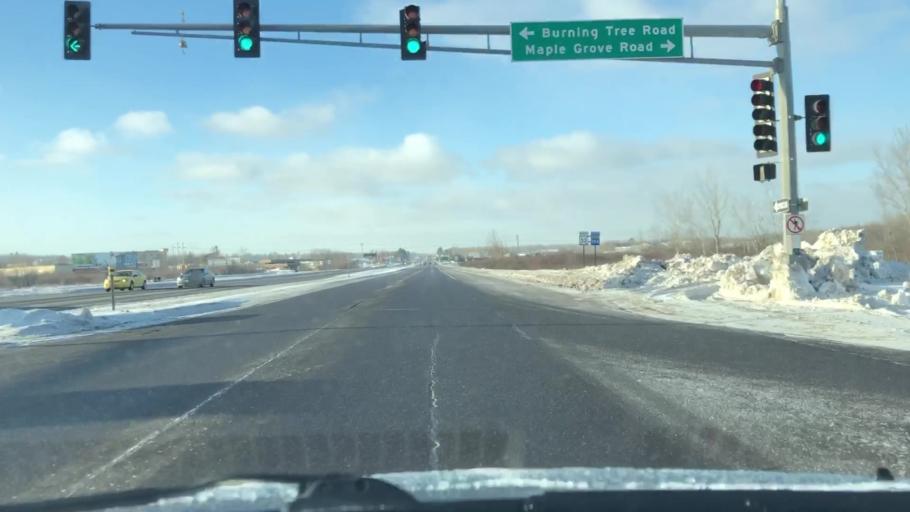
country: US
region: Minnesota
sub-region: Saint Louis County
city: Duluth
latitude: 46.8109
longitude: -92.1683
